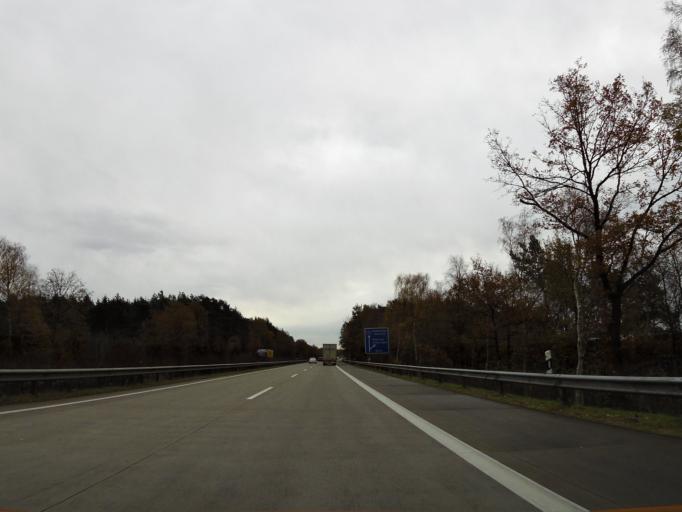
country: DE
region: Lower Saxony
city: Walsrode
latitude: 52.8417
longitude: 9.5826
